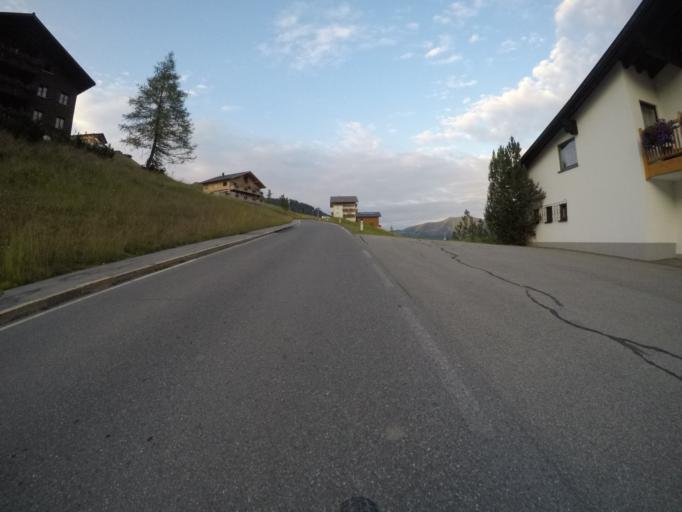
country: AT
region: Vorarlberg
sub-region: Politischer Bezirk Bregenz
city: Damuels
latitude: 47.2808
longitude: 9.8816
